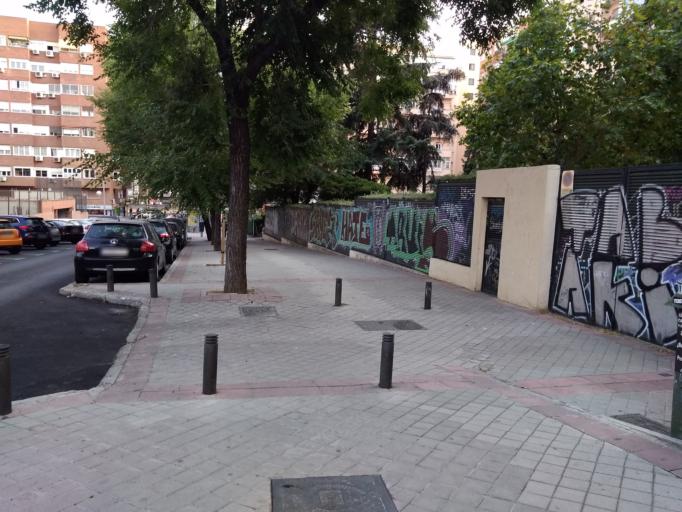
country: ES
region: Madrid
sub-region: Provincia de Madrid
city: Retiro
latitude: 40.4080
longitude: -3.6689
